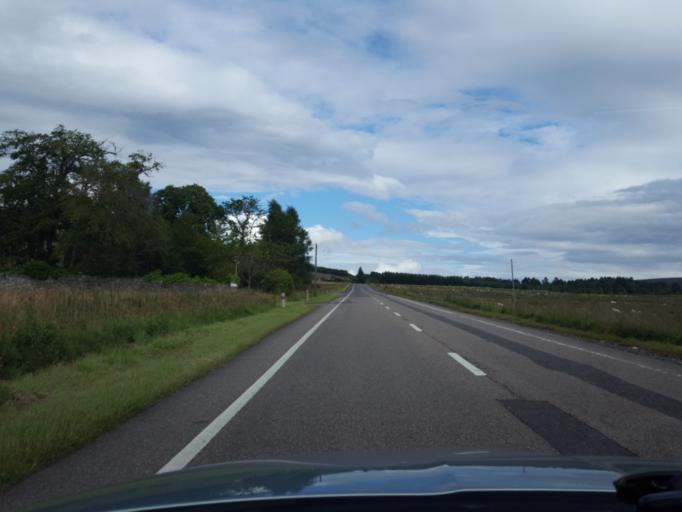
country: GB
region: Scotland
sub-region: Moray
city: Rothes
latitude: 57.4305
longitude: -3.3368
